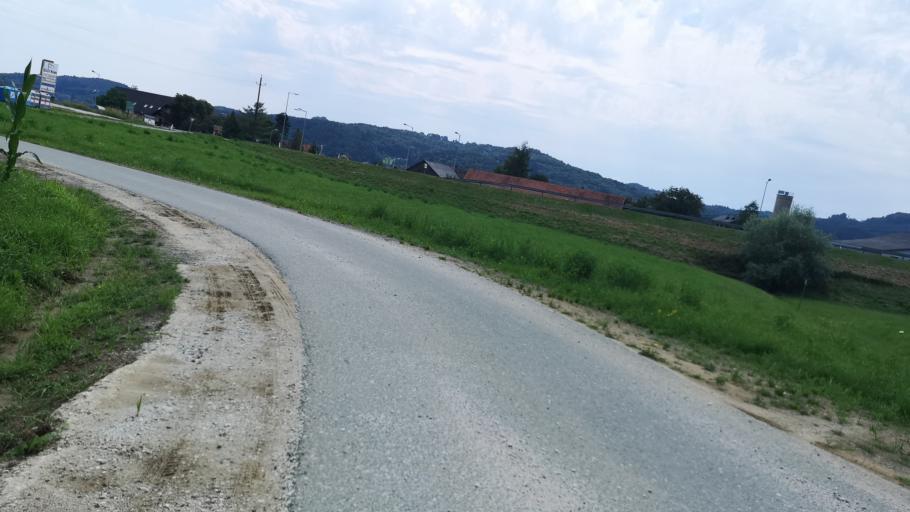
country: AT
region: Styria
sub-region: Politischer Bezirk Leibnitz
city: Weitendorf
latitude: 46.8676
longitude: 15.4648
